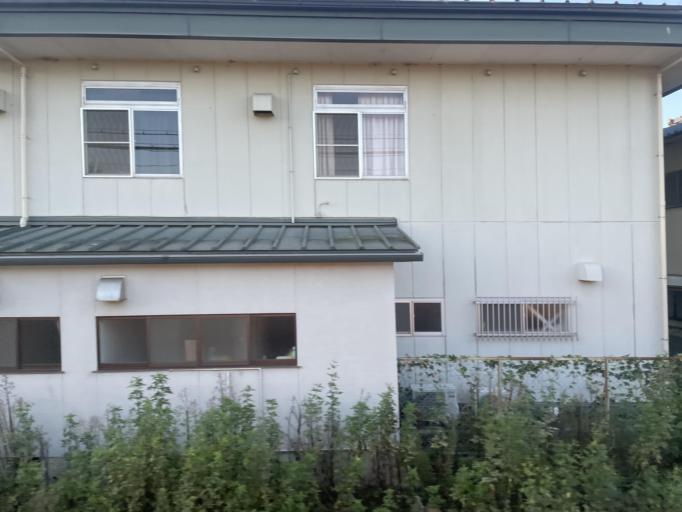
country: JP
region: Nara
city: Kashihara-shi
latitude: 34.5126
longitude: 135.8182
